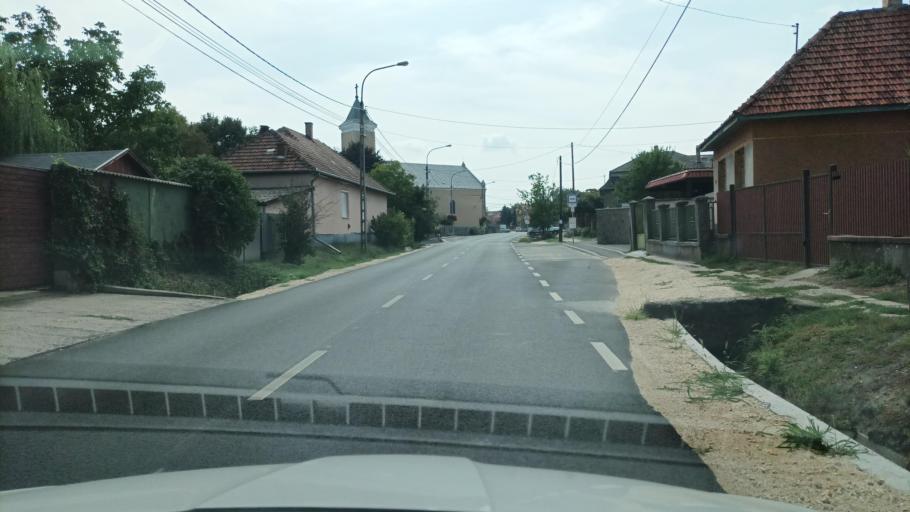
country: HU
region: Pest
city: Tura
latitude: 47.6139
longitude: 19.5975
